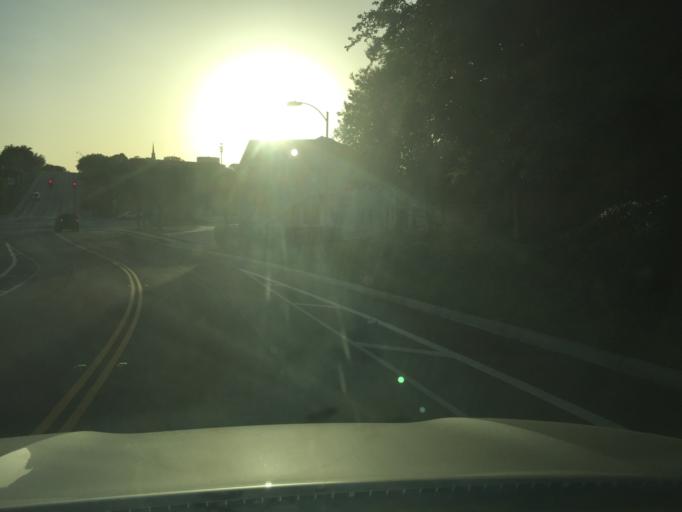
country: US
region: Texas
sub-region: Bexar County
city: Hollywood Park
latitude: 29.6325
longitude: -98.4943
